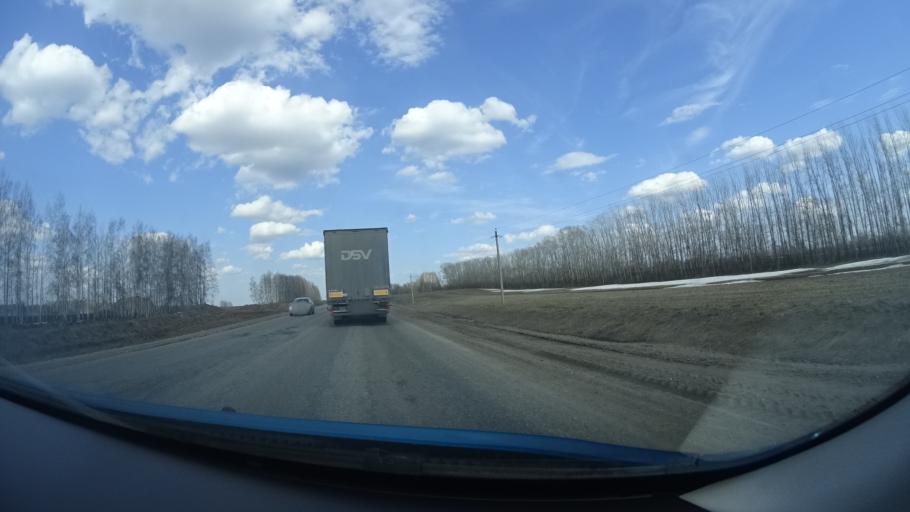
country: RU
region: Bashkortostan
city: Buzdyak
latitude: 54.6883
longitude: 54.8146
